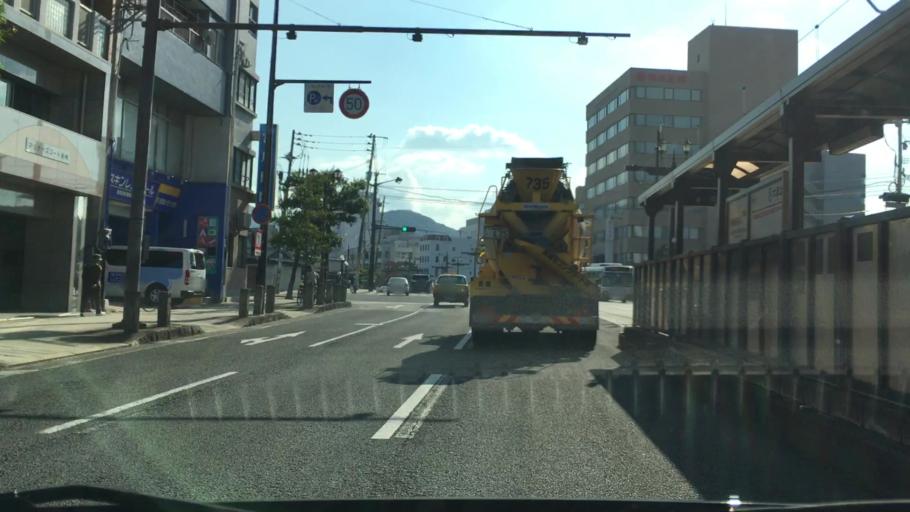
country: JP
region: Nagasaki
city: Nagasaki-shi
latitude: 32.7455
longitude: 129.8721
